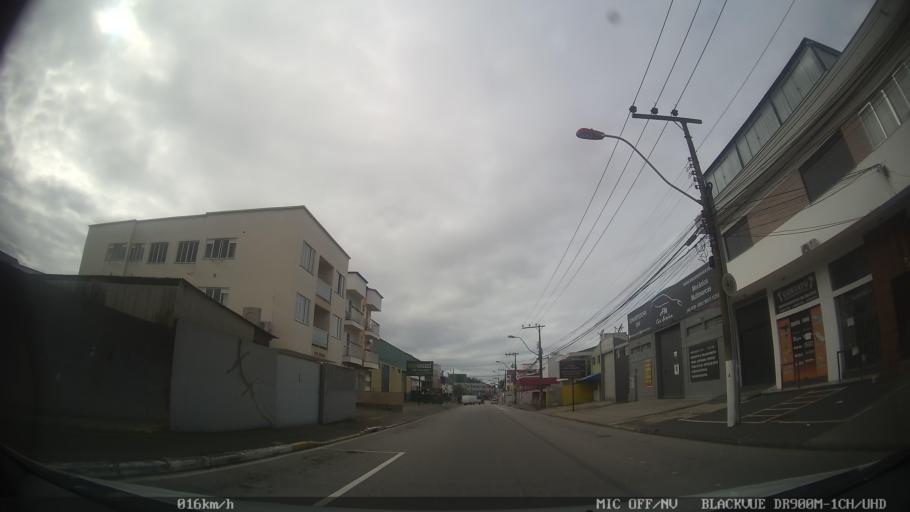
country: BR
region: Santa Catarina
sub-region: Sao Jose
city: Campinas
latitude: -27.5545
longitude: -48.6222
